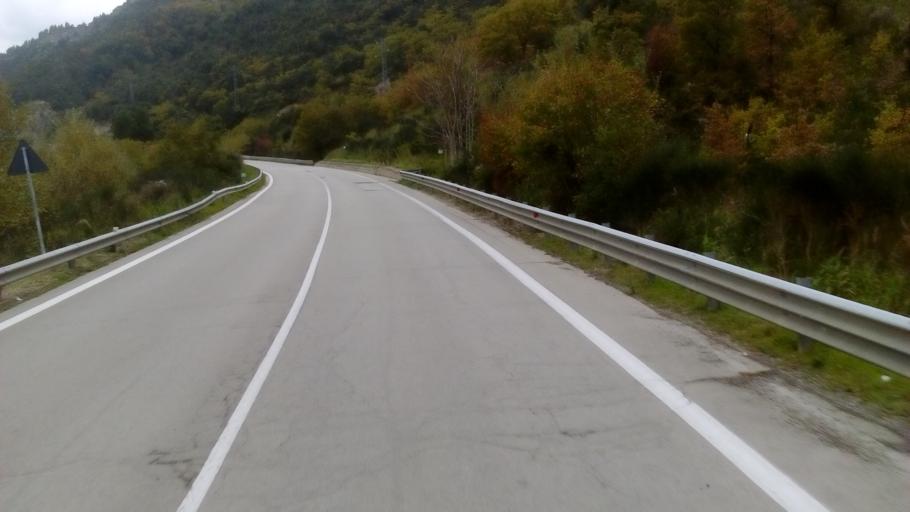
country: IT
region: Molise
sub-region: Provincia di Campobasso
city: Roccavivara
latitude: 41.8470
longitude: 14.5878
